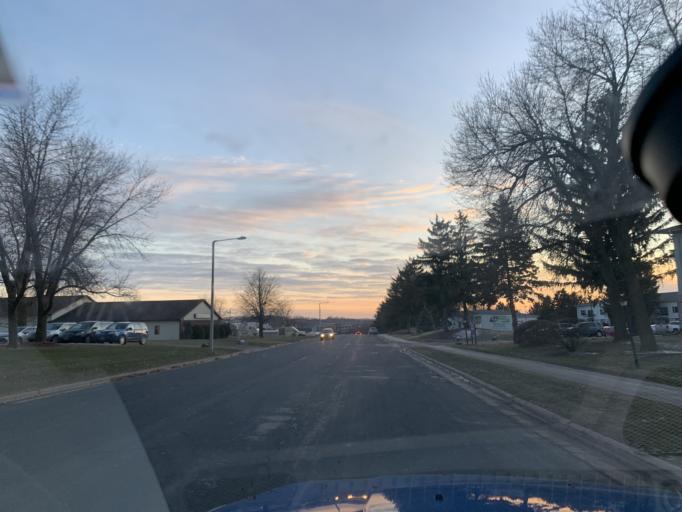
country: US
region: Wisconsin
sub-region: Dane County
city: Shorewood Hills
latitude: 43.0228
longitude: -89.4716
